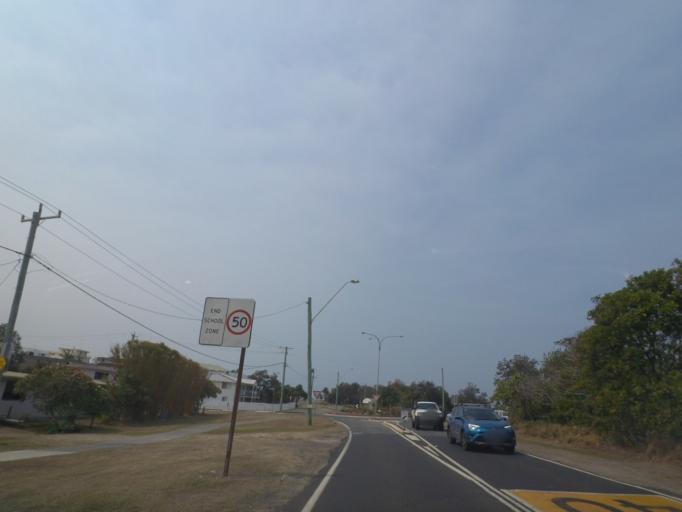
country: AU
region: New South Wales
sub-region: Tweed
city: Casuarina
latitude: -28.3370
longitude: 153.5739
